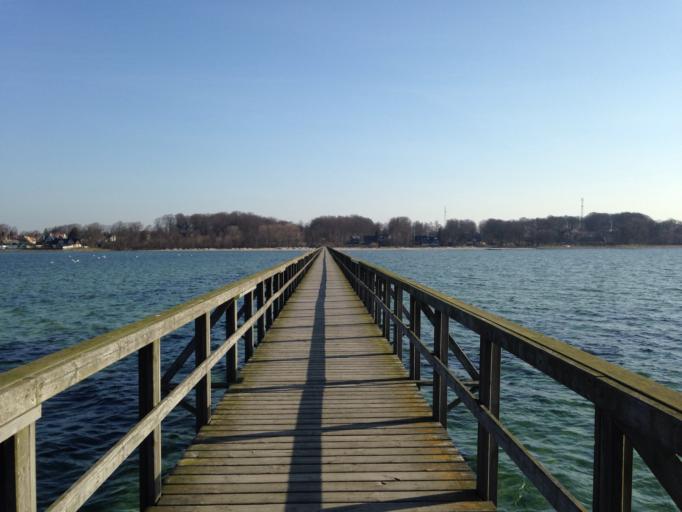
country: SE
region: Skane
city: Bjarred
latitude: 55.7084
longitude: 13.0196
